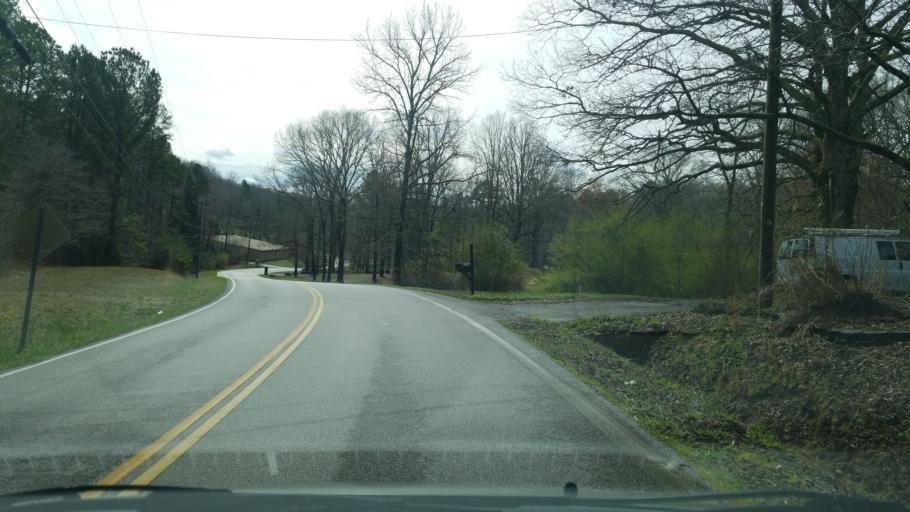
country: US
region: Tennessee
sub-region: Hamilton County
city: Harrison
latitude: 35.1366
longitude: -85.0851
